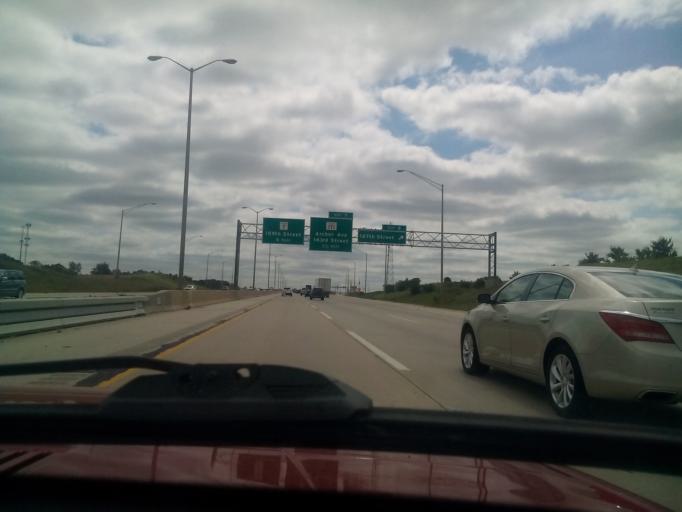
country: US
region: Illinois
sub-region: Cook County
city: Lemont
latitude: 41.6629
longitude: -88.0239
